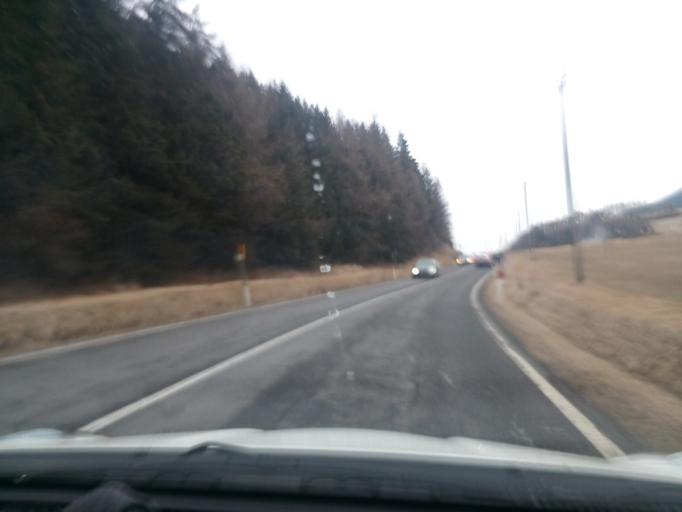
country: IT
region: Trentino-Alto Adige
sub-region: Bolzano
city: Curon Venosta
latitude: 46.8377
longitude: 10.5079
